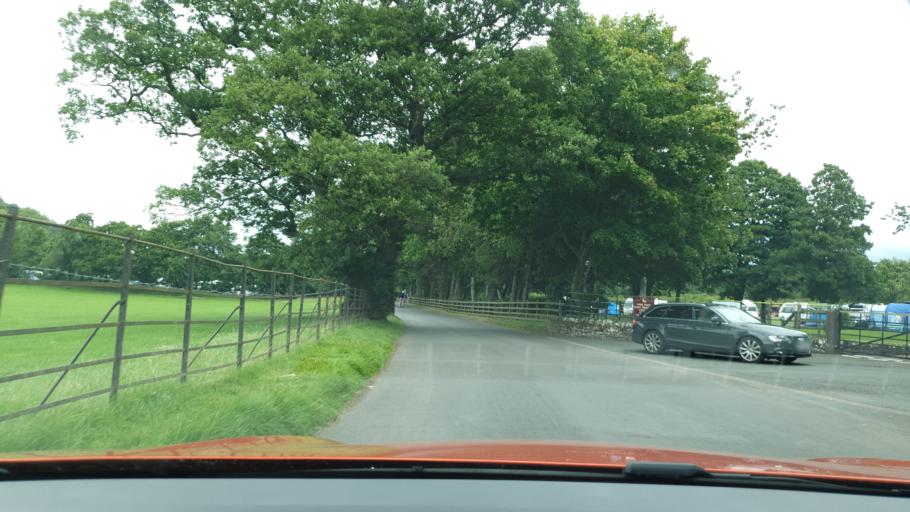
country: GB
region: England
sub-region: Cumbria
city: Penrith
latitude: 54.6032
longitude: -2.8244
